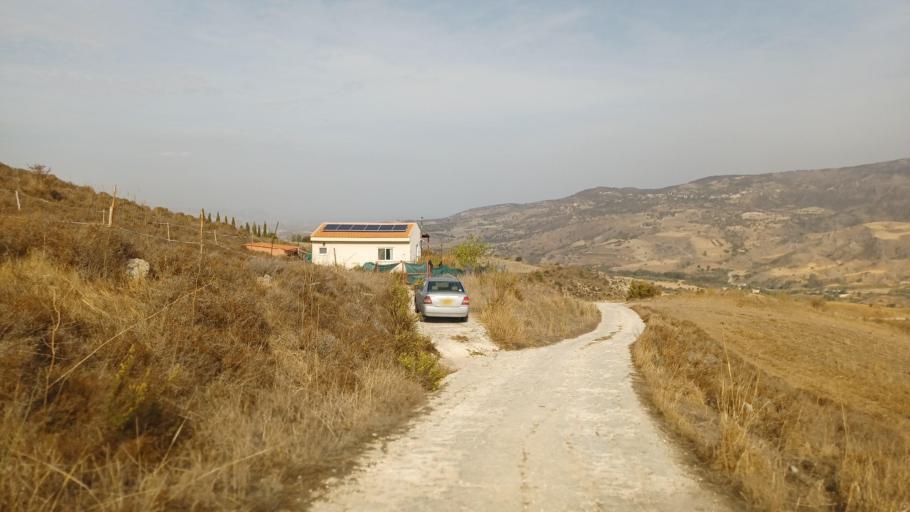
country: CY
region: Pafos
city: Tala
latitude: 34.9394
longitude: 32.5162
